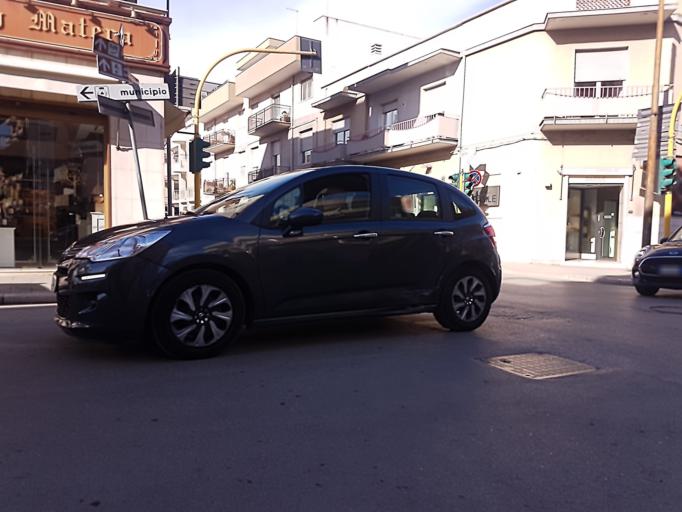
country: IT
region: Apulia
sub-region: Provincia di Barletta - Andria - Trani
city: Andria
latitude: 41.2328
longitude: 16.2949
